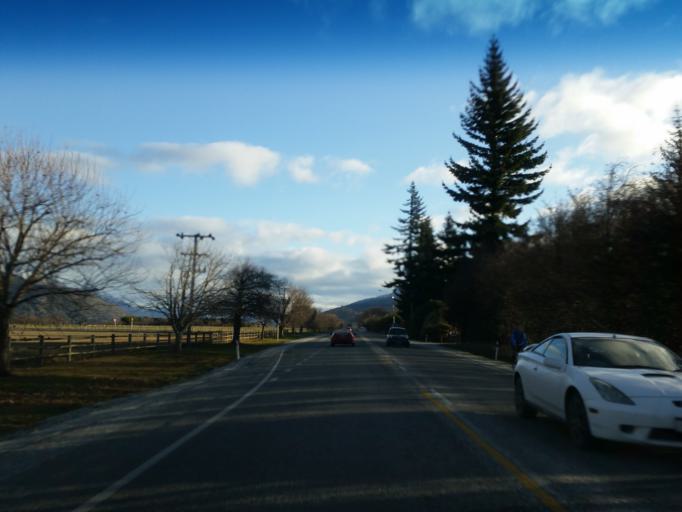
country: NZ
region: Otago
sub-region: Queenstown-Lakes District
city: Arrowtown
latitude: -44.9971
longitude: 168.7845
